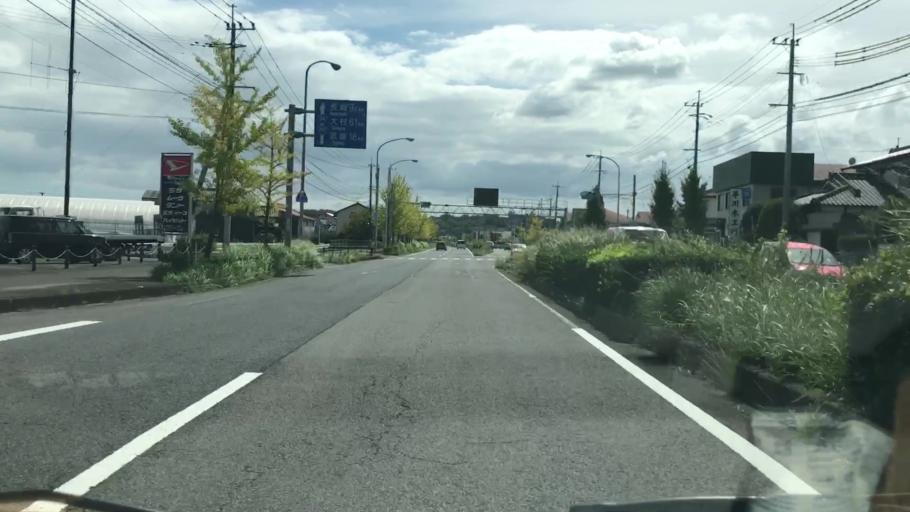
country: JP
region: Saga Prefecture
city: Saga-shi
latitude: 33.2410
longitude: 130.1848
